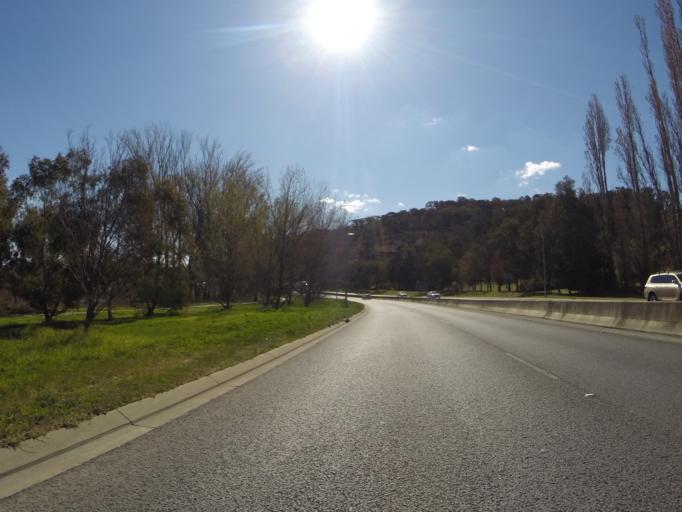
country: AU
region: Australian Capital Territory
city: Forrest
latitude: -35.3027
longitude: 149.1609
